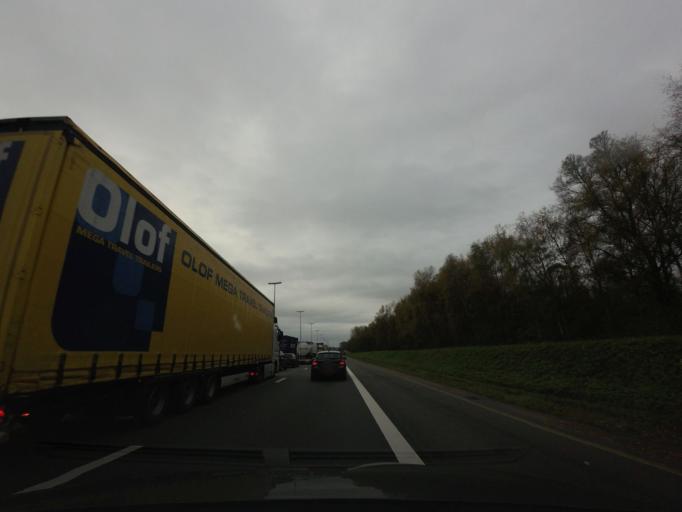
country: BE
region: Flanders
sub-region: Provincie Antwerpen
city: Zwijndrecht
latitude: 51.2236
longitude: 4.3517
